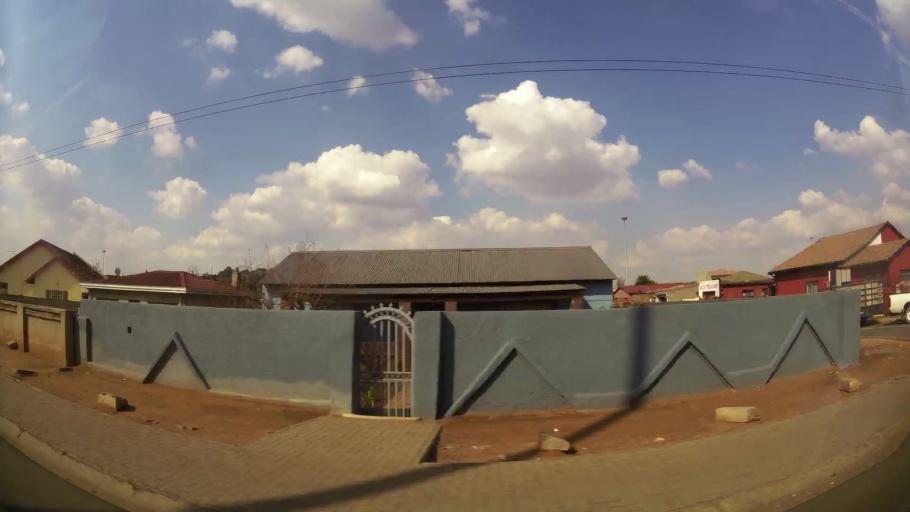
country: ZA
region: Gauteng
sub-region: Ekurhuleni Metropolitan Municipality
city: Germiston
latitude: -26.3093
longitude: 28.1576
